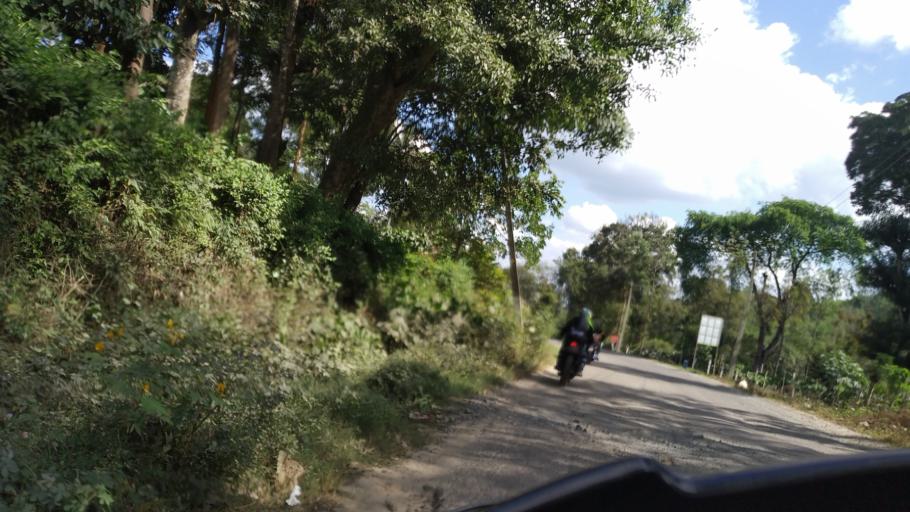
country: IN
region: Karnataka
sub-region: Kodagu
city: Ponnampet
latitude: 11.9656
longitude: 76.0553
